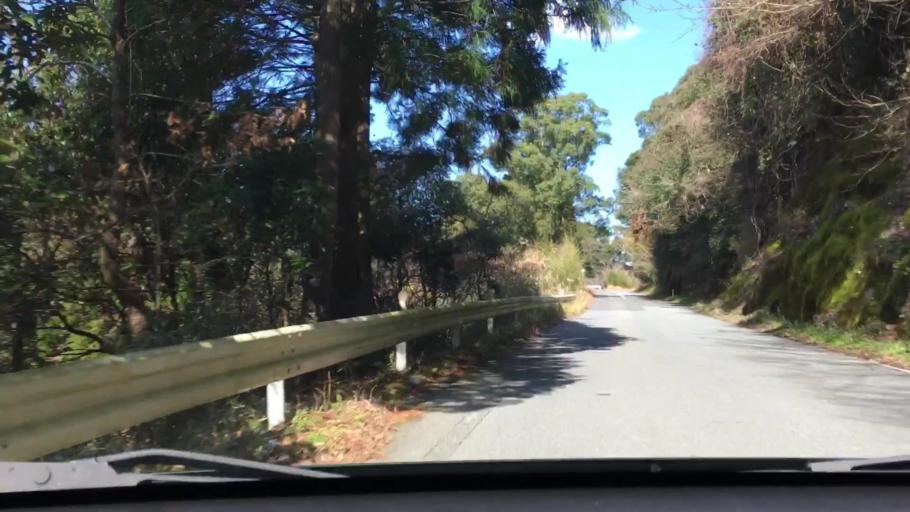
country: JP
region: Kagoshima
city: Ijuin
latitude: 31.7160
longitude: 130.4130
